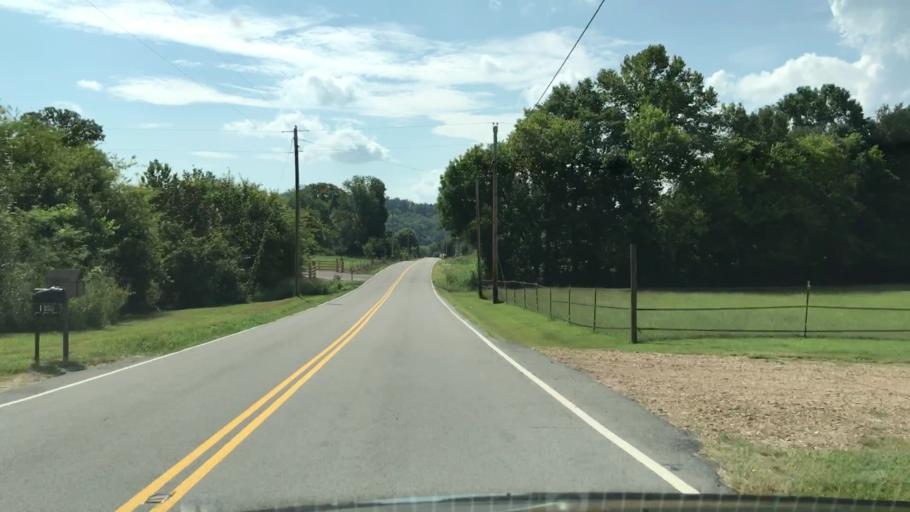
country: US
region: Tennessee
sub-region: Trousdale County
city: Hartsville
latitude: 36.4713
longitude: -86.1786
